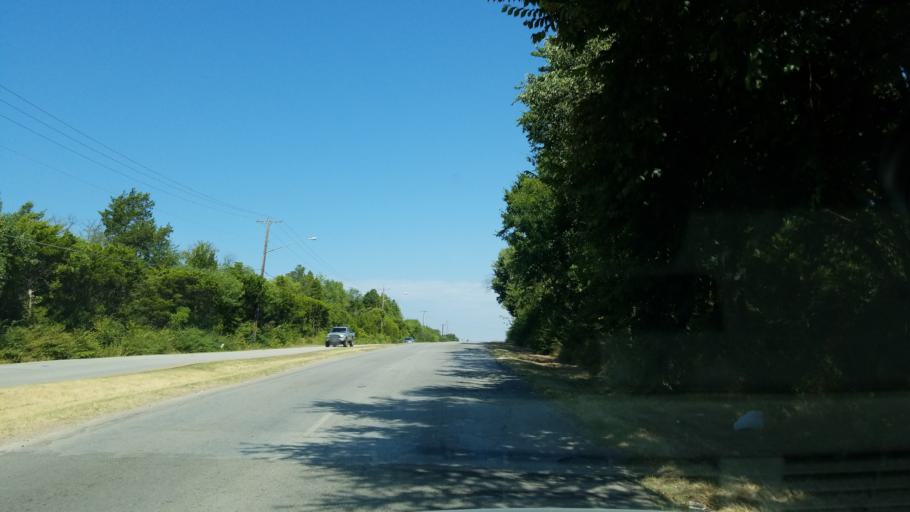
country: US
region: Texas
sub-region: Dallas County
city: Cockrell Hill
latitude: 32.7381
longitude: -96.8985
